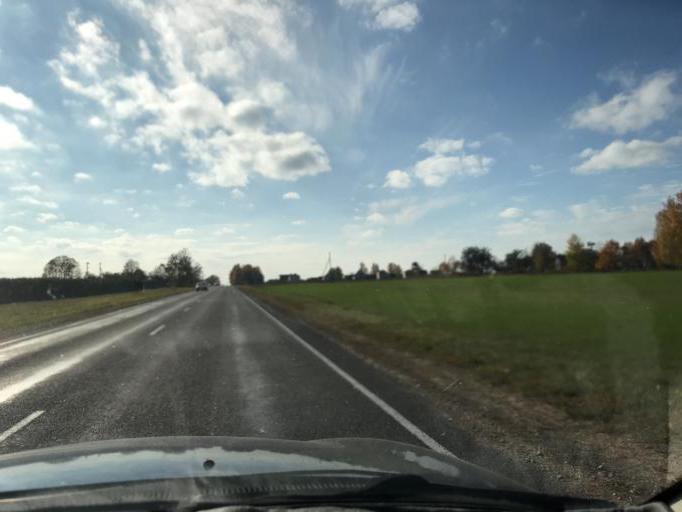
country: BY
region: Grodnenskaya
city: Voranava
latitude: 54.1711
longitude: 25.3322
